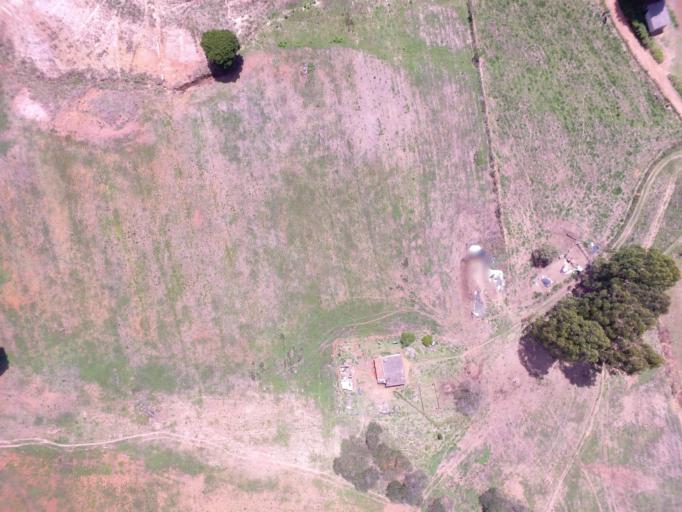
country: BR
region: Minas Gerais
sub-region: Barroso
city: Barroso
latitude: -21.0401
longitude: -44.0028
